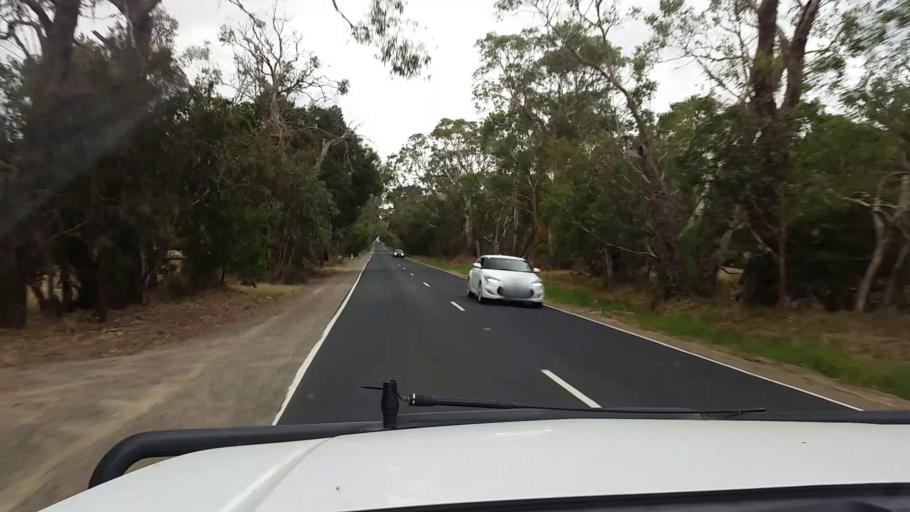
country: AU
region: Victoria
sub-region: Mornington Peninsula
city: Somerville
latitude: -38.2313
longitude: 145.1523
